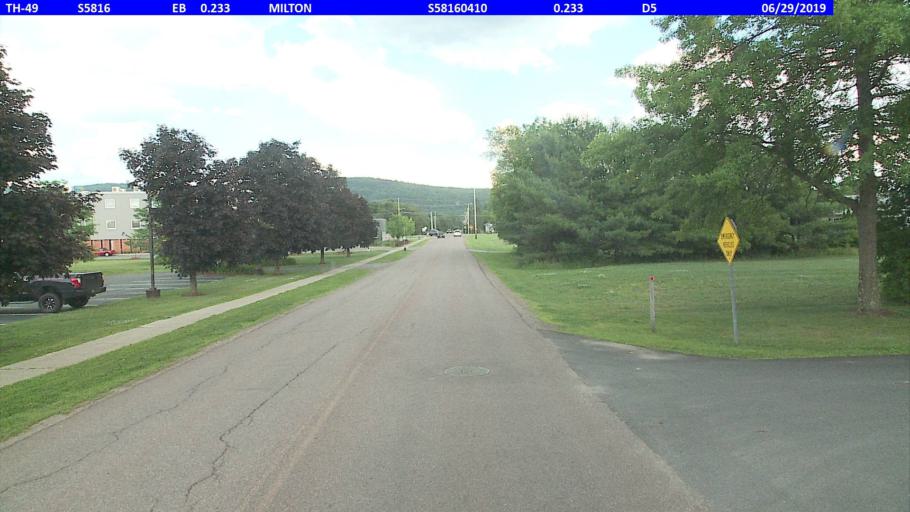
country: US
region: Vermont
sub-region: Chittenden County
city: Milton
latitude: 44.6191
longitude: -73.1224
